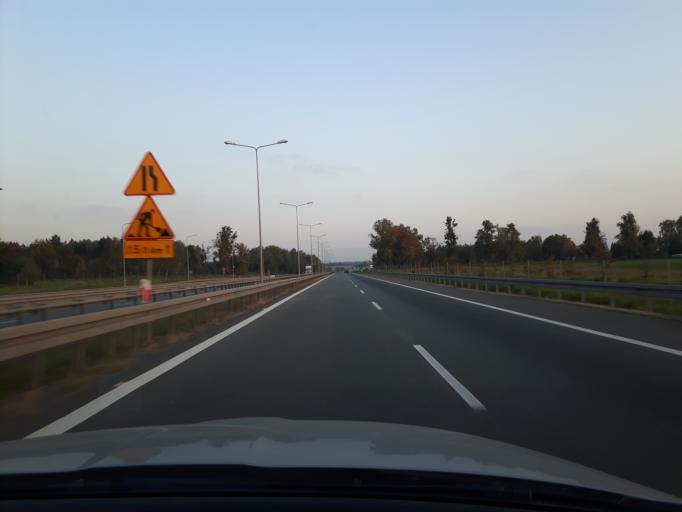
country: PL
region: Warmian-Masurian Voivodeship
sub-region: Powiat elblaski
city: Paslek
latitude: 54.0773
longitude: 19.6112
